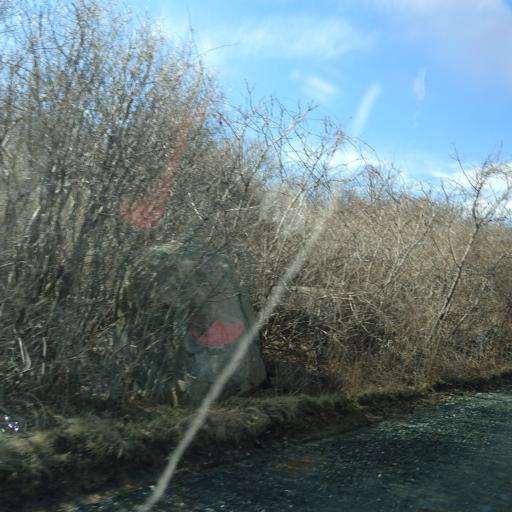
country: US
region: Massachusetts
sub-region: Essex County
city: Ipswich
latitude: 42.7046
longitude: -70.7740
